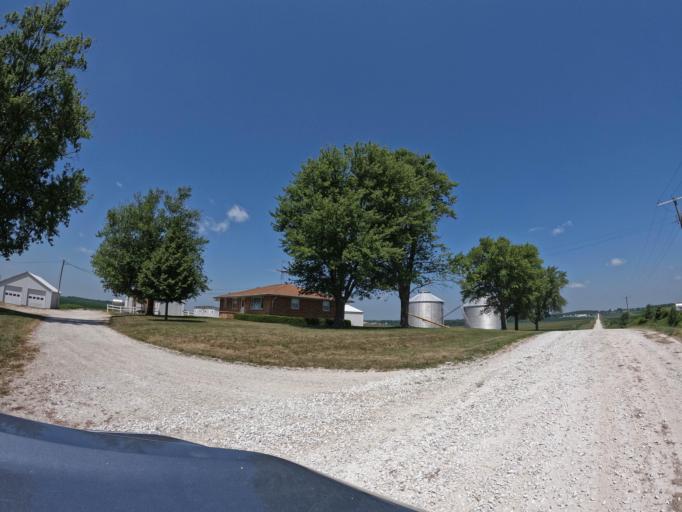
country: US
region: Iowa
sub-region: Keokuk County
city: Sigourney
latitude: 41.2814
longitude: -92.2189
